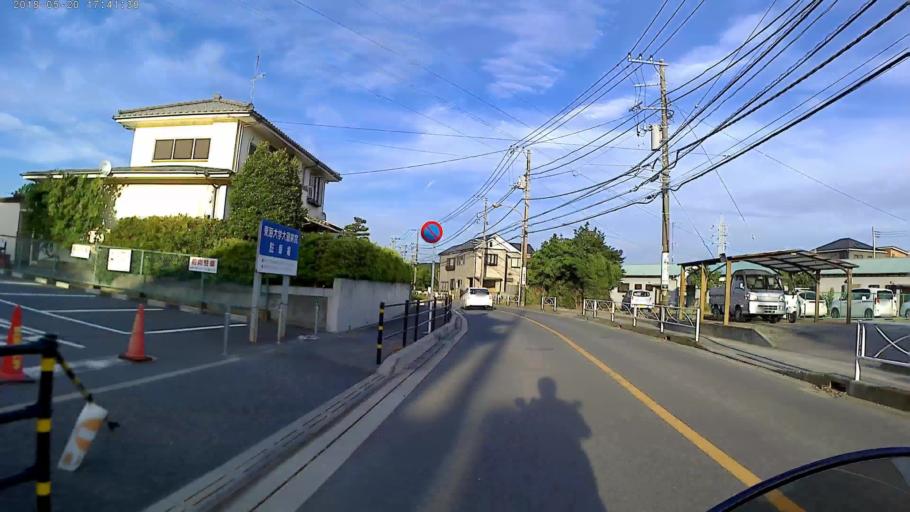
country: JP
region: Kanagawa
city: Ninomiya
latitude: 35.3095
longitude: 139.2756
